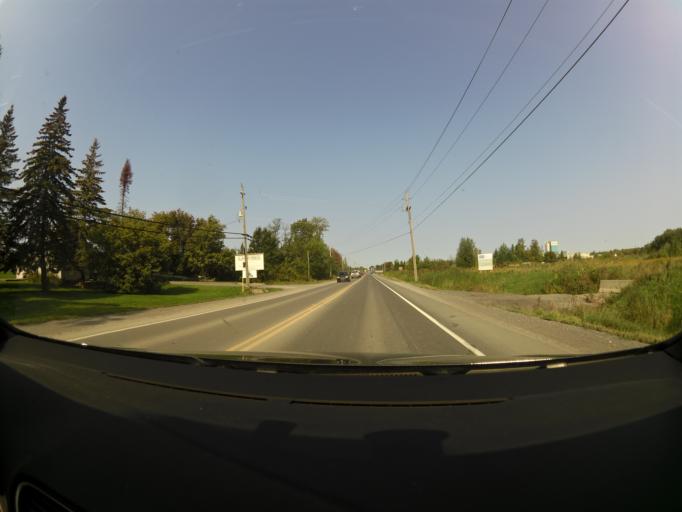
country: CA
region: Ontario
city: Bells Corners
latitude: 45.2891
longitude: -75.9671
